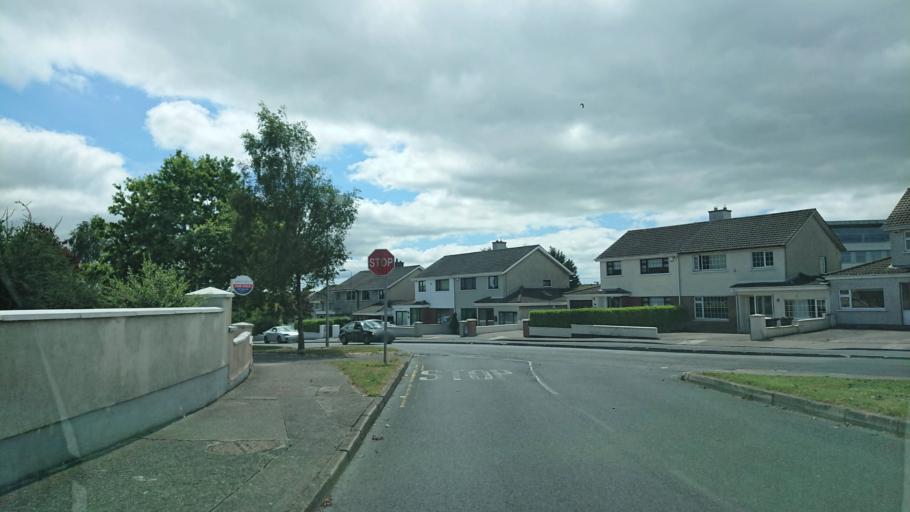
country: IE
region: Munster
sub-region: Waterford
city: Waterford
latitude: 52.2468
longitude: -7.1352
